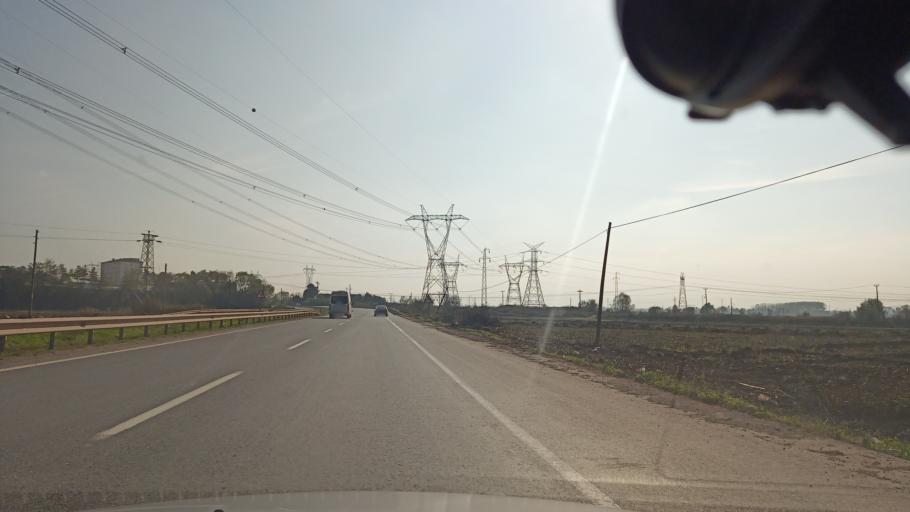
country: TR
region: Sakarya
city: Adapazari
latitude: 40.8259
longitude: 30.3909
